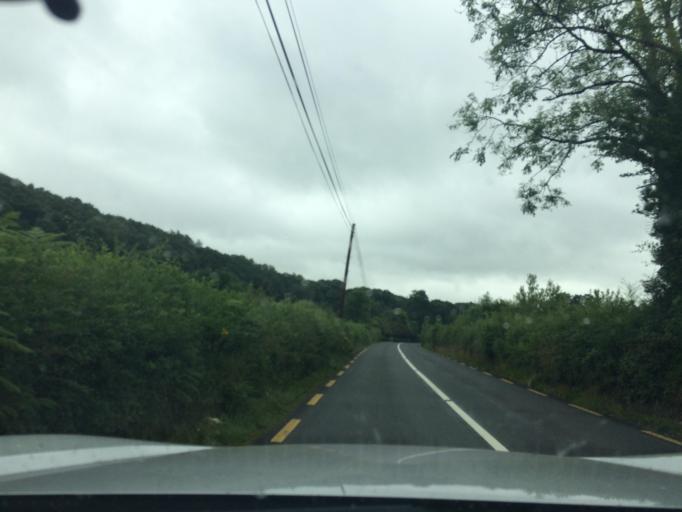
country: IE
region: Munster
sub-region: South Tipperary
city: Cluain Meala
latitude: 52.3307
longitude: -7.7299
